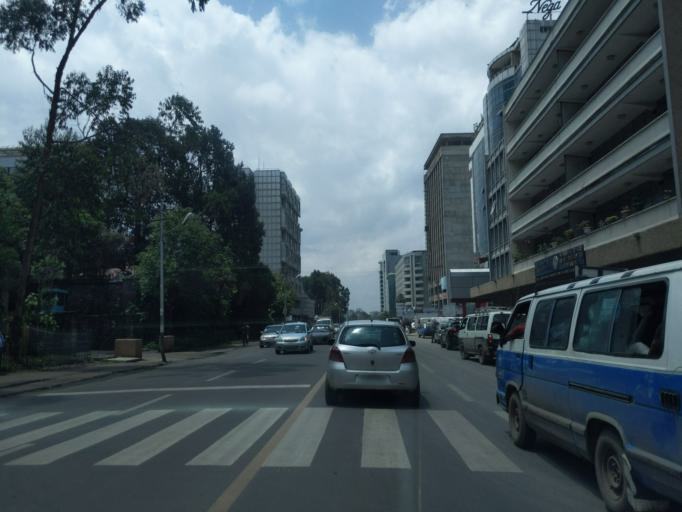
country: ET
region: Adis Abeba
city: Addis Ababa
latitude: 9.0169
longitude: 38.7650
